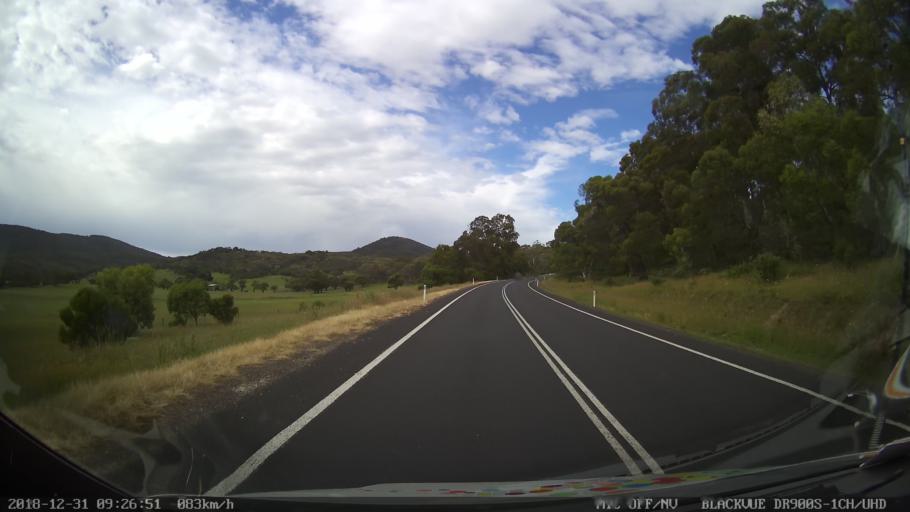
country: AU
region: New South Wales
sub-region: Snowy River
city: Jindabyne
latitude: -36.4527
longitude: 148.4925
